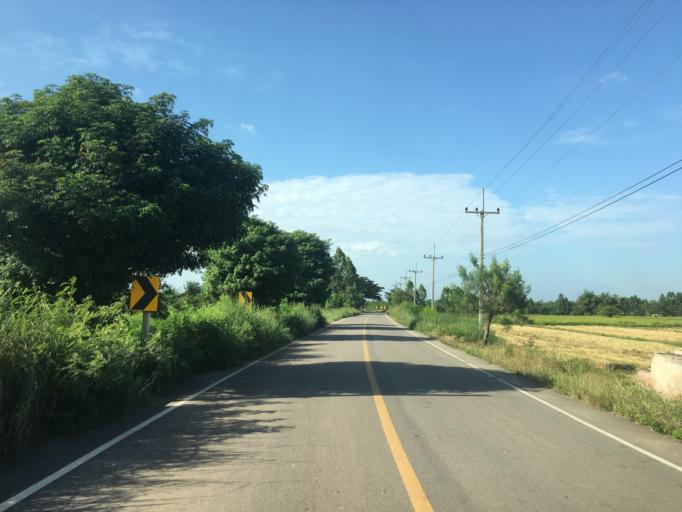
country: TH
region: Chiang Rai
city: Pa Daet
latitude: 19.4339
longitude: 100.0103
